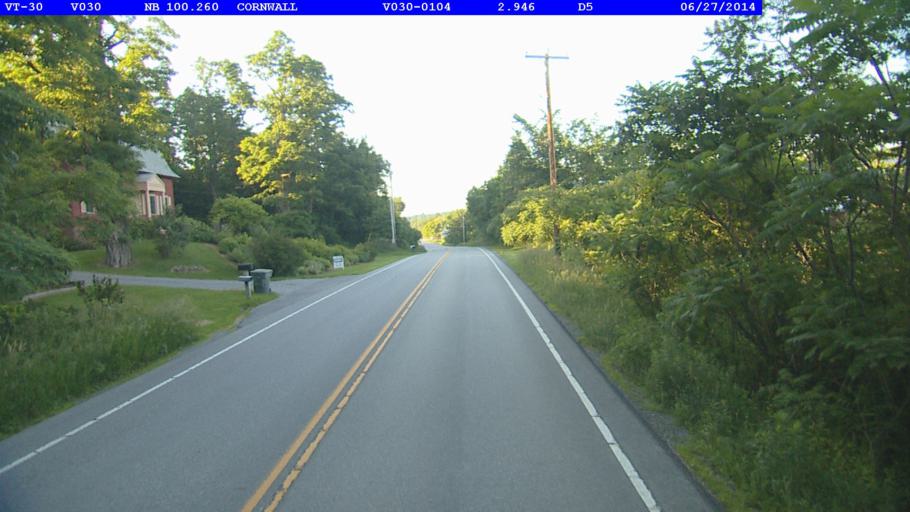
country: US
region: Vermont
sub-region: Addison County
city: Middlebury (village)
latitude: 43.9501
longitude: -73.2103
